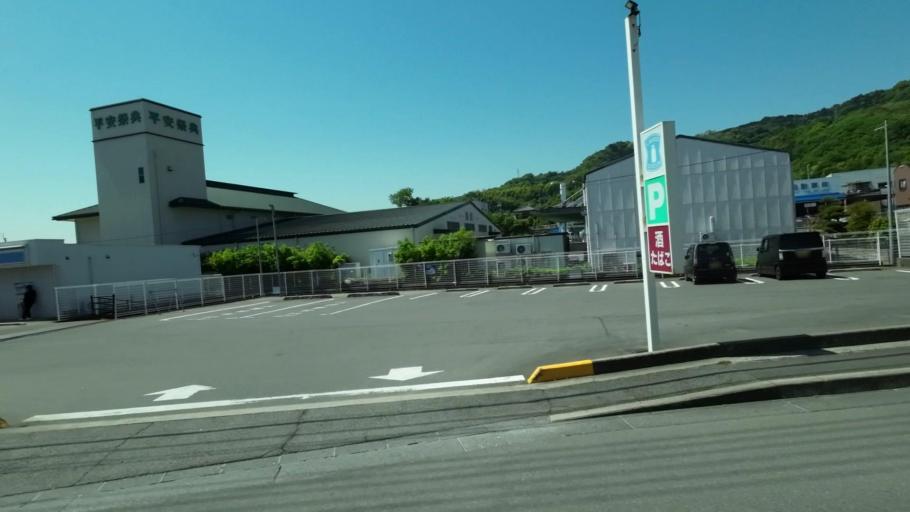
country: JP
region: Ehime
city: Hojo
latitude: 34.0903
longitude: 132.9828
